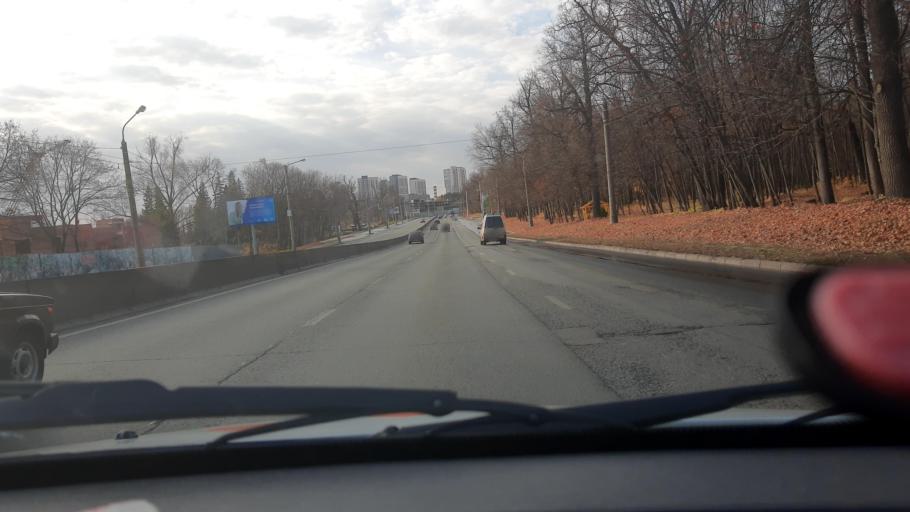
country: RU
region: Bashkortostan
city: Ufa
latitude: 54.7334
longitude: 56.0259
